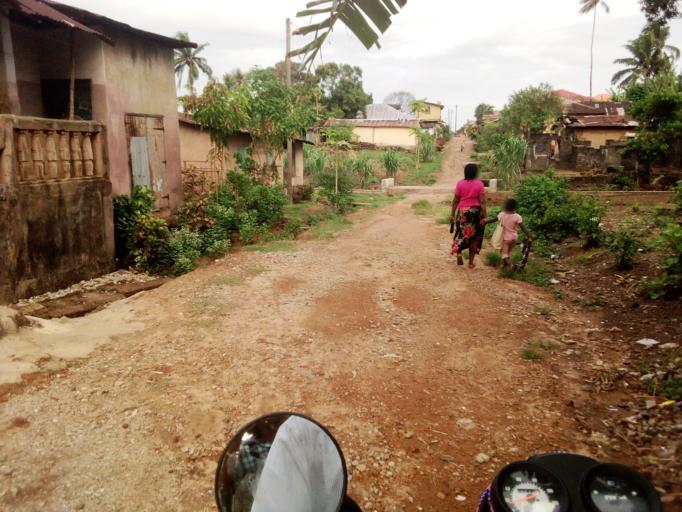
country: SL
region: Western Area
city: Waterloo
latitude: 8.3362
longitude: -13.0699
